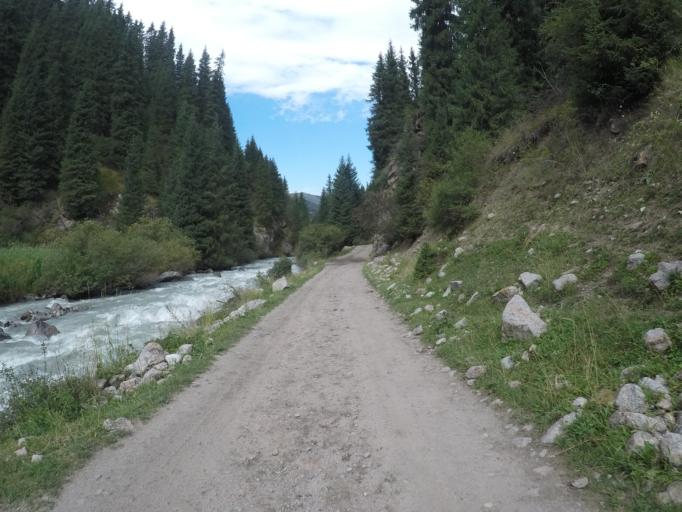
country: KG
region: Ysyk-Koel
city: Teploklyuchenka
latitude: 42.4418
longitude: 78.5551
